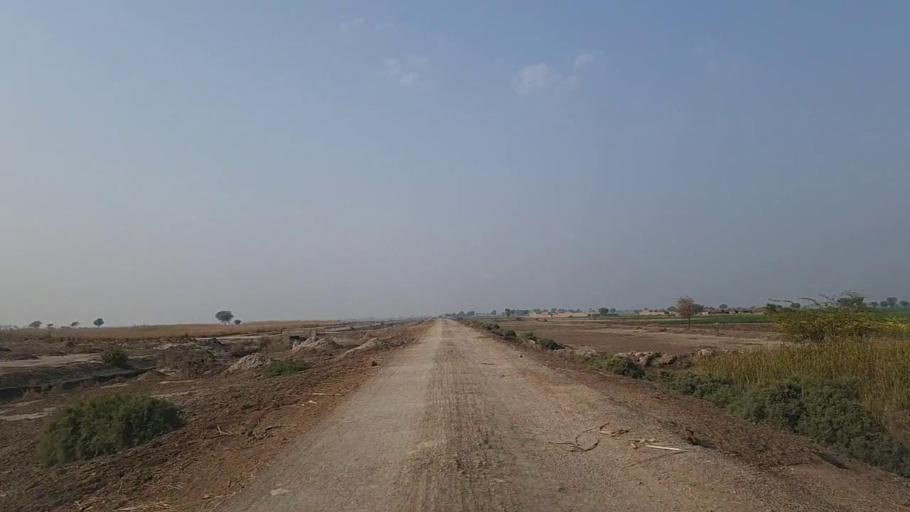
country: PK
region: Sindh
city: Nawabshah
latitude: 26.3311
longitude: 68.4759
